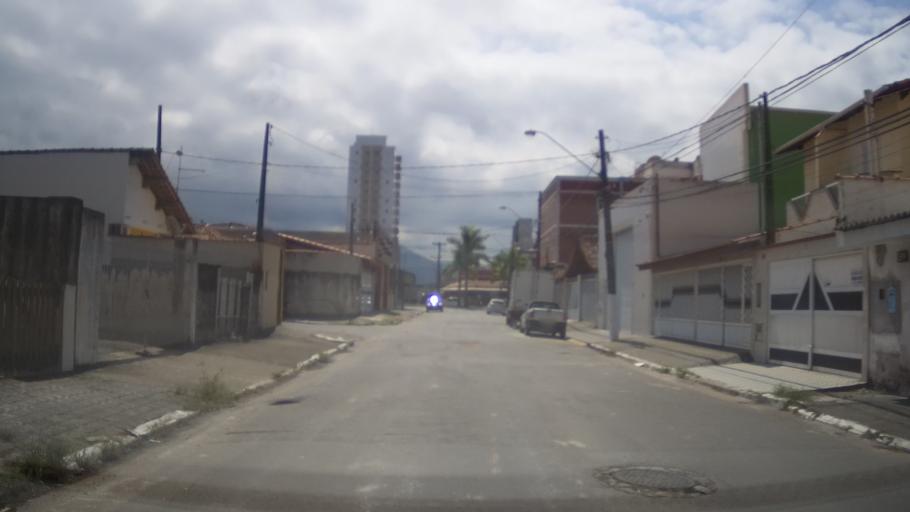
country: BR
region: Sao Paulo
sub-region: Praia Grande
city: Praia Grande
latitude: -24.0188
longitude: -46.4577
